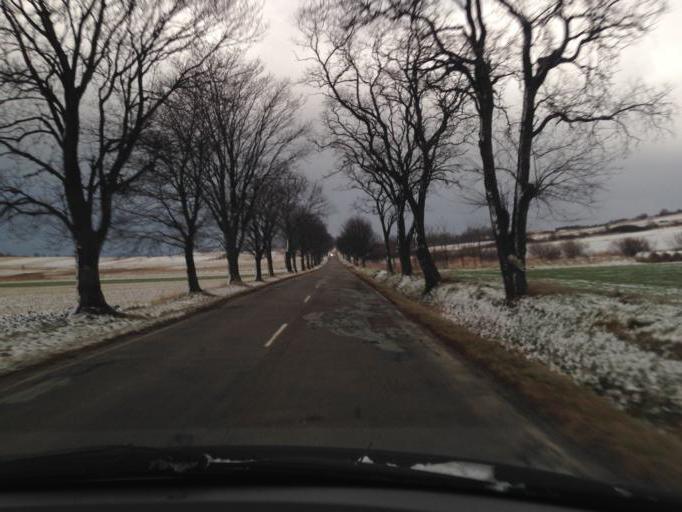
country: PL
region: Subcarpathian Voivodeship
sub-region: Powiat jasielski
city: Osiek Jasielski
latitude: 49.6106
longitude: 21.4888
